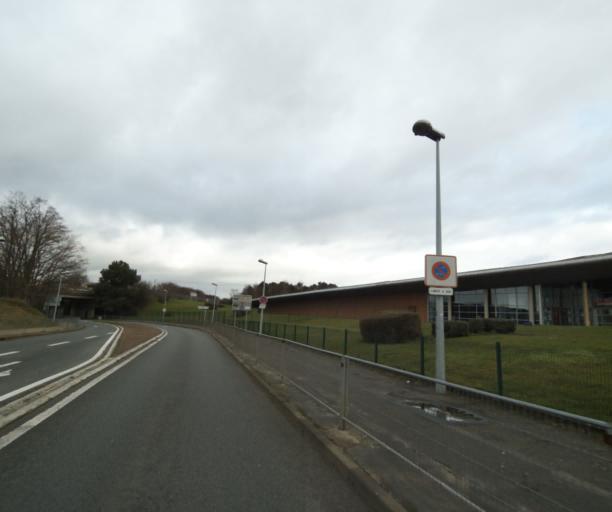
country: FR
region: Pays de la Loire
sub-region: Departement de la Sarthe
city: Arnage
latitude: 47.9566
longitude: 0.2076
